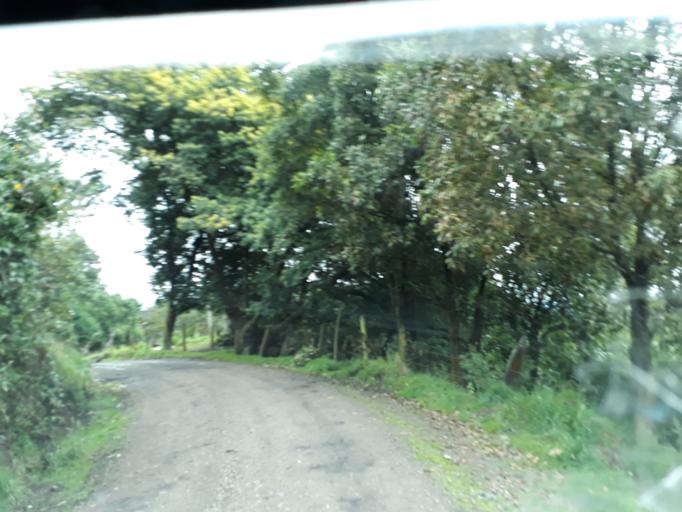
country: CO
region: Cundinamarca
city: Cogua
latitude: 5.1613
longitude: -73.9907
